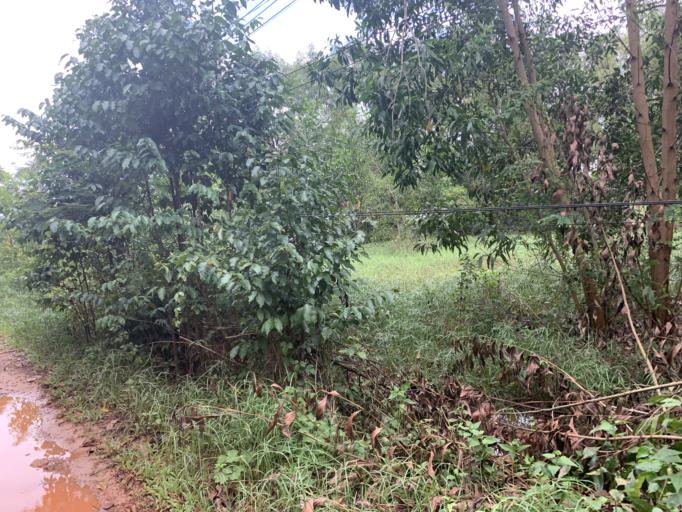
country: KH
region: Koh Kong
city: Koh Kong
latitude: 11.6223
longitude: 102.9817
